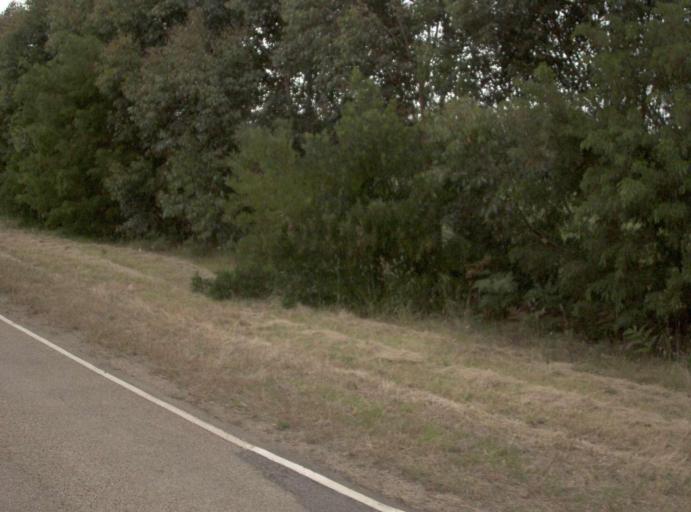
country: AU
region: Victoria
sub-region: Wellington
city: Sale
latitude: -38.0048
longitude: 147.2660
